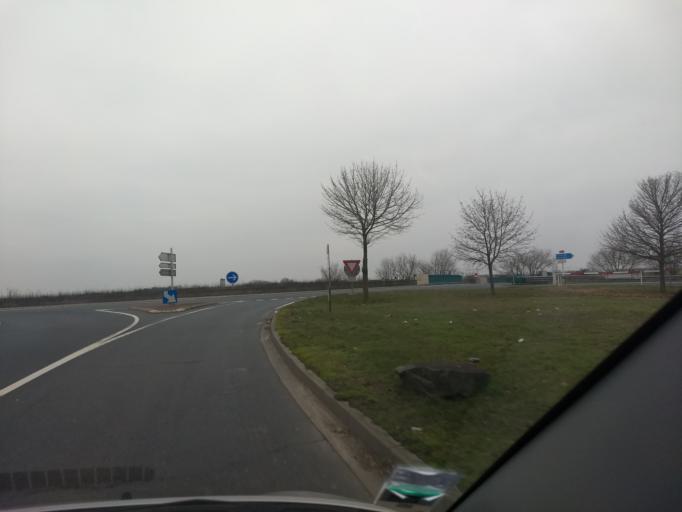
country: FR
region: Centre
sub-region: Departement de l'Indre
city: Deols
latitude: 46.8518
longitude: 1.7023
